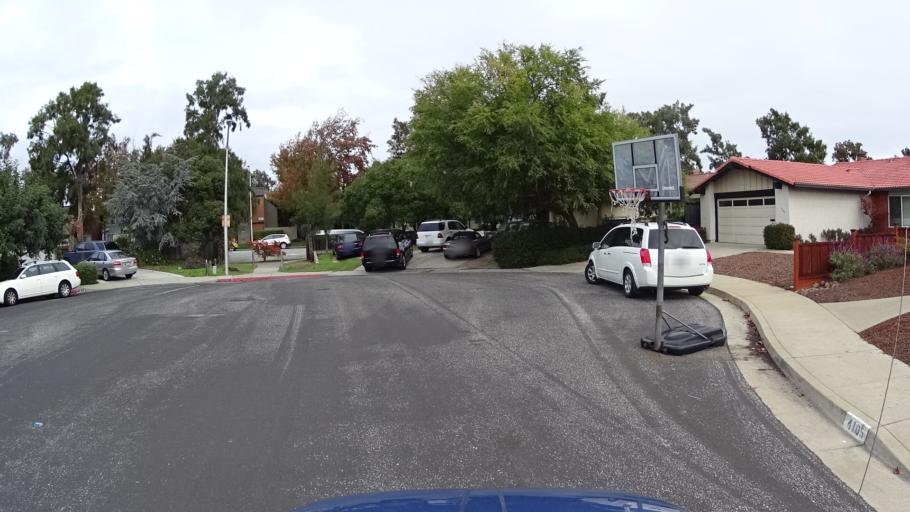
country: US
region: California
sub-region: San Mateo County
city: Belmont
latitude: 37.5314
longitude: -122.2830
